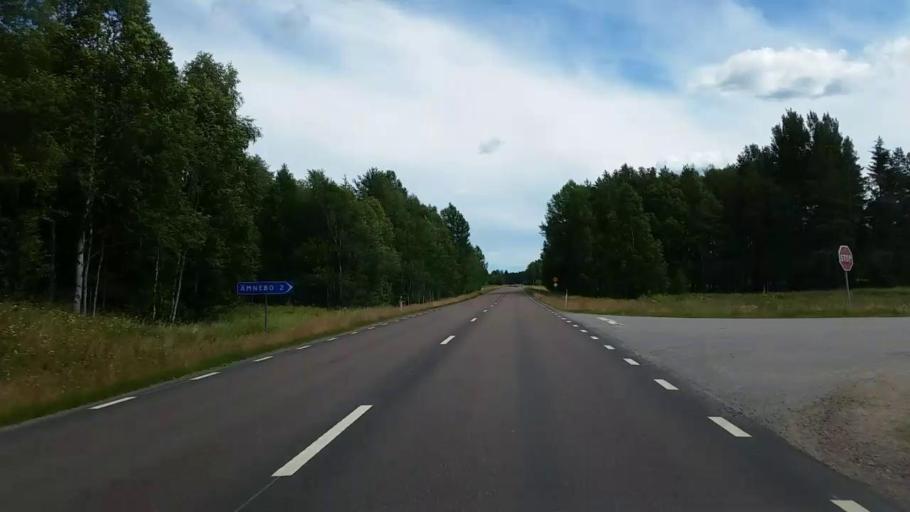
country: SE
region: Gaevleborg
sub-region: Ovanakers Kommun
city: Edsbyn
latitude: 61.3660
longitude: 15.8778
